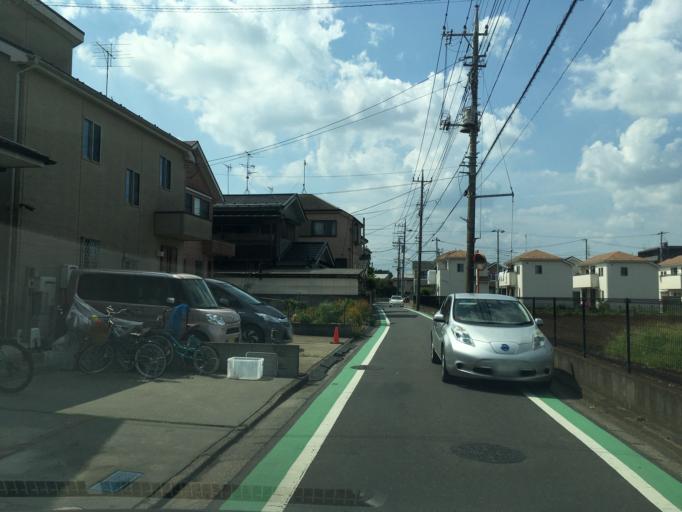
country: JP
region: Tokyo
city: Higashimurayama-shi
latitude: 35.7685
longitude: 139.4820
